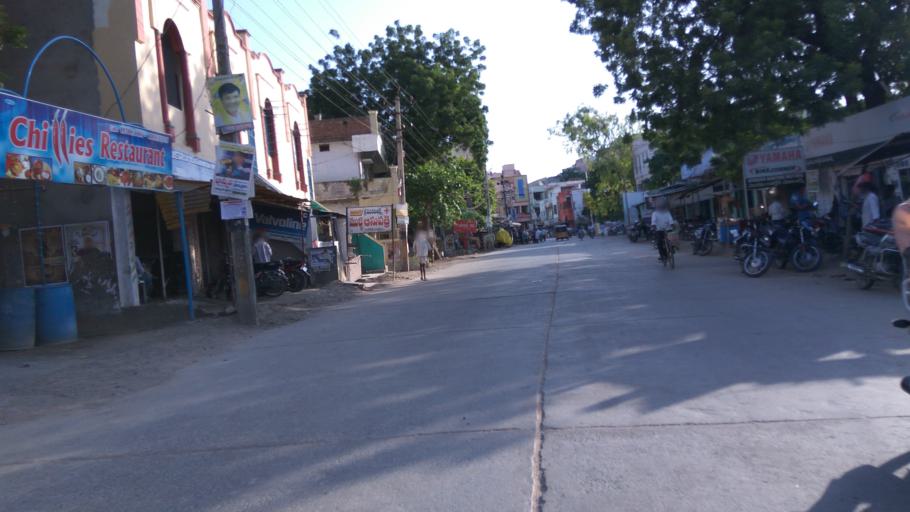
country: IN
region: Andhra Pradesh
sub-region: Prakasam
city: Markapur
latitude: 15.7418
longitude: 79.2734
